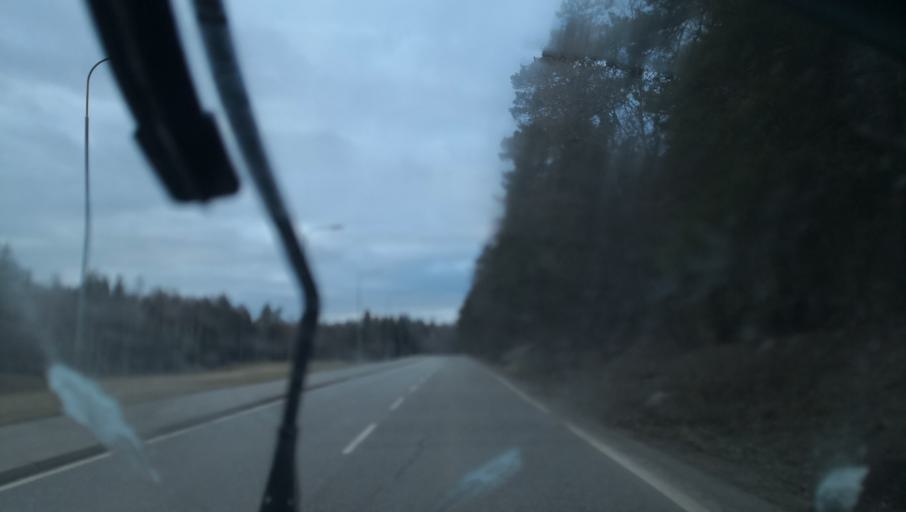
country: SE
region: Stockholm
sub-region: Varmdo Kommun
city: Gustavsberg
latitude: 59.3370
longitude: 18.3783
